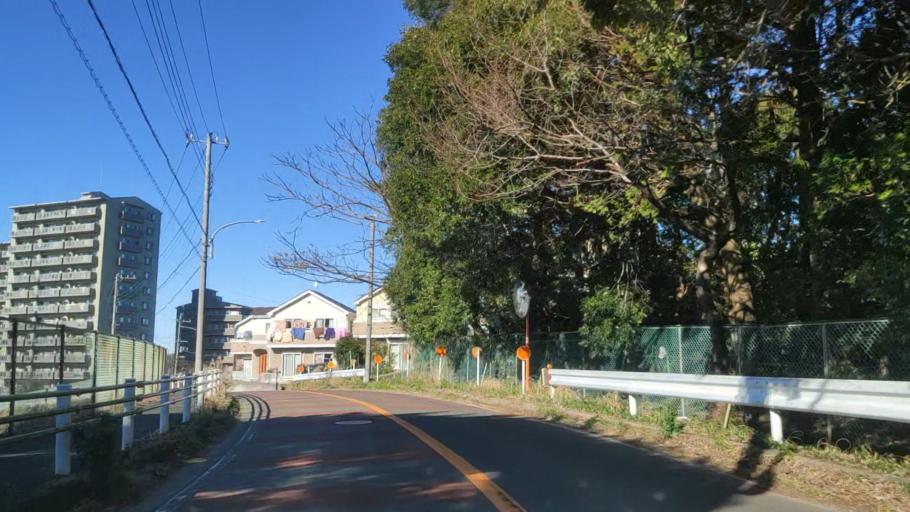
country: JP
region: Kanagawa
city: Minami-rinkan
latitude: 35.5059
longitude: 139.5348
